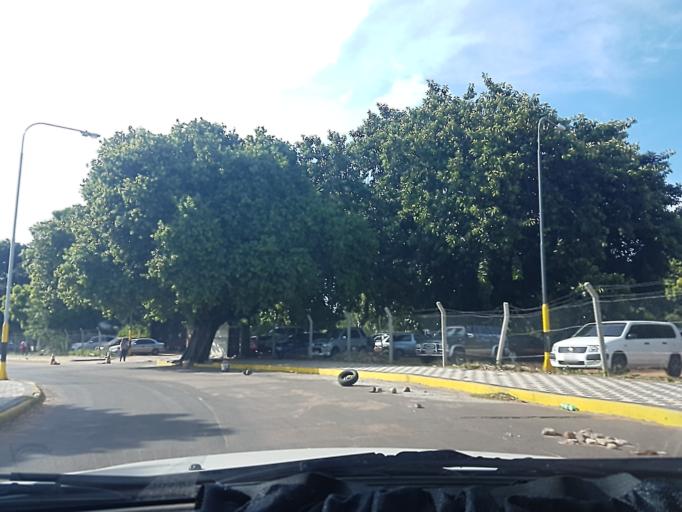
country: PY
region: Asuncion
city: Asuncion
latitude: -25.2716
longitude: -57.5818
